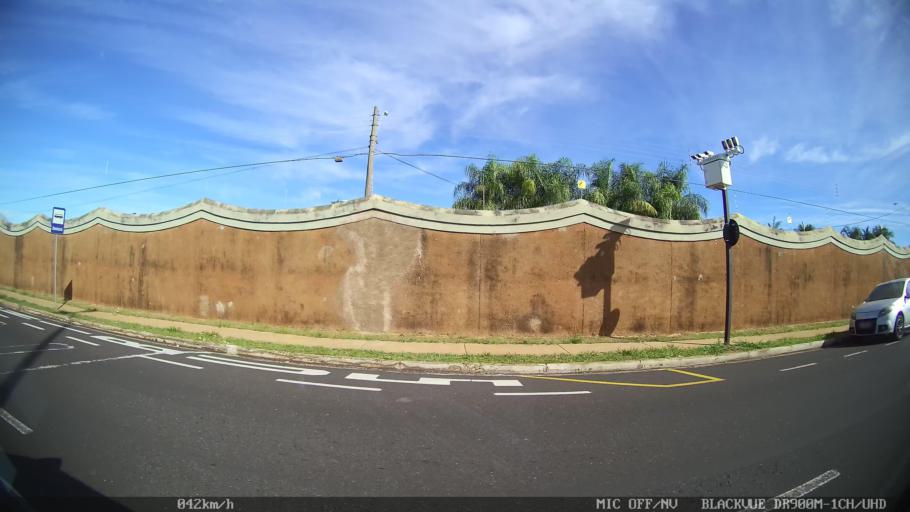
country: BR
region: Sao Paulo
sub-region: Sao Jose Do Rio Preto
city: Sao Jose do Rio Preto
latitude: -20.8083
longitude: -49.3470
